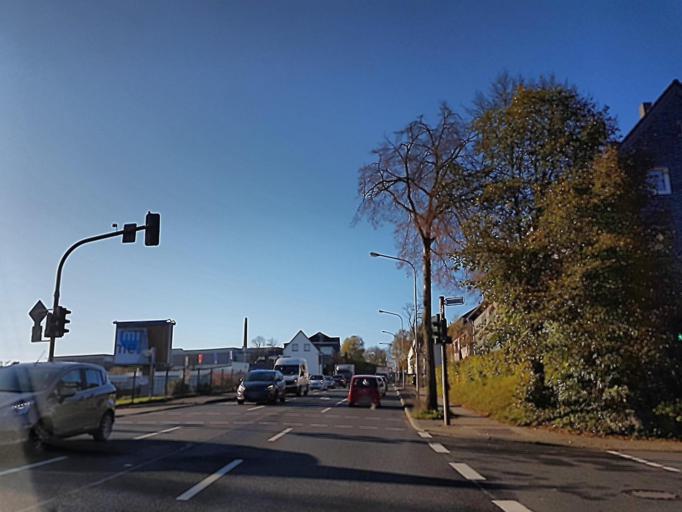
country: DE
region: North Rhine-Westphalia
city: Wermelskirchen
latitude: 51.1873
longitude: 7.2634
